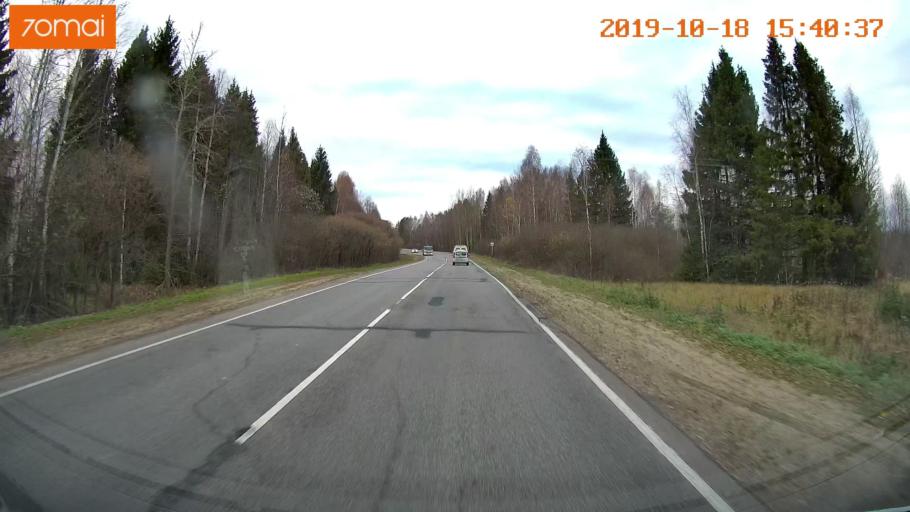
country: RU
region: Vladimir
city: Golovino
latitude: 55.9365
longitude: 40.5927
